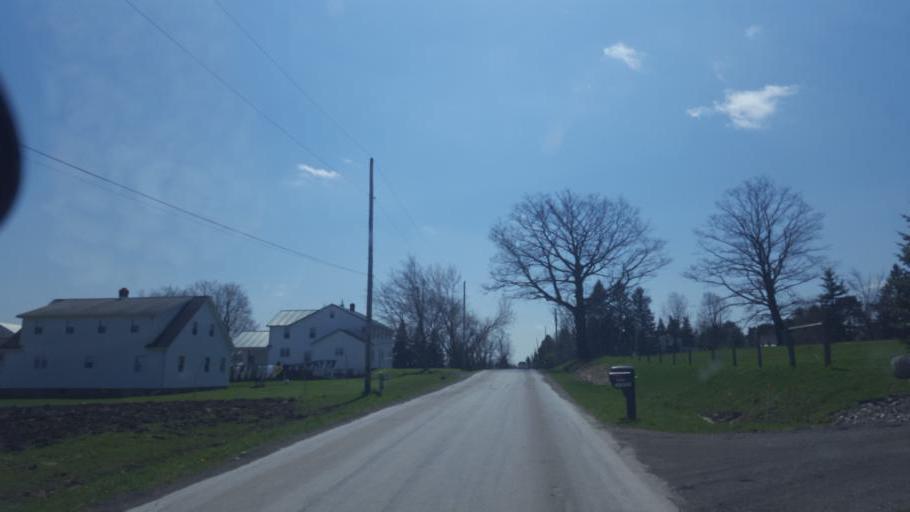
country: US
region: Ohio
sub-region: Geauga County
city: Middlefield
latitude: 41.4305
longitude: -81.0805
